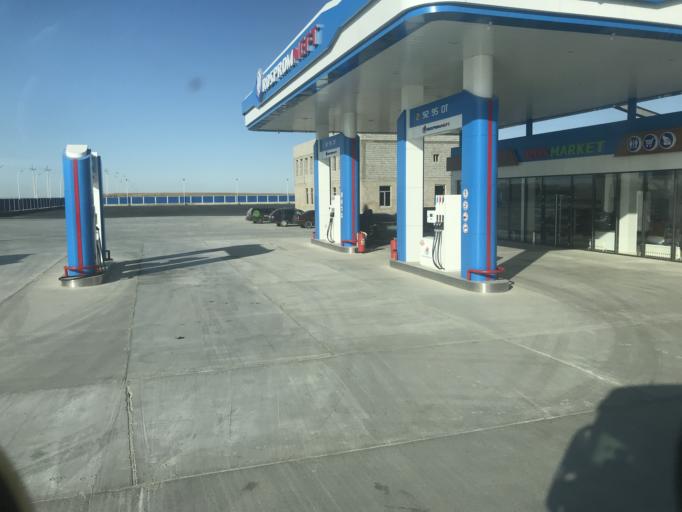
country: KZ
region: Ongtustik Qazaqstan
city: Temirlanovka
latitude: 42.5704
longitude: 69.3112
